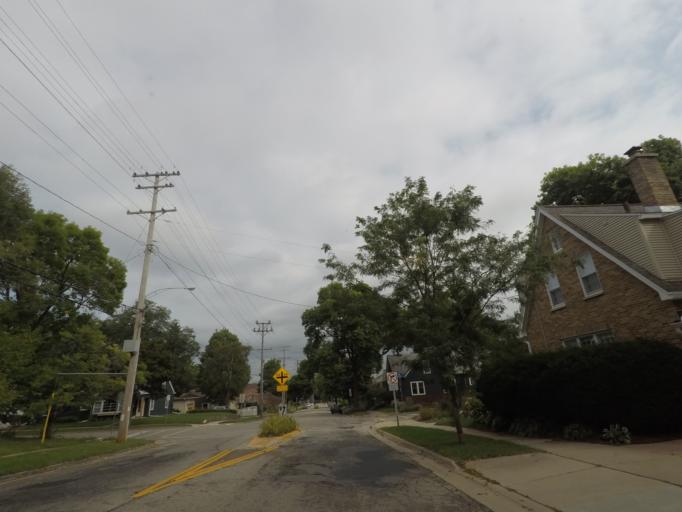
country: US
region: Wisconsin
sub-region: Dane County
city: Shorewood Hills
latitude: 43.0712
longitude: -89.4362
